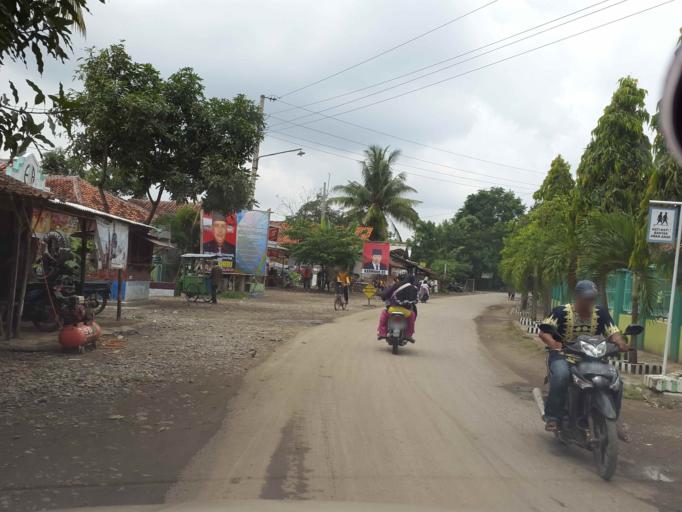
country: ID
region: Central Java
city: Bulakamba
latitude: -6.9675
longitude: 108.9900
